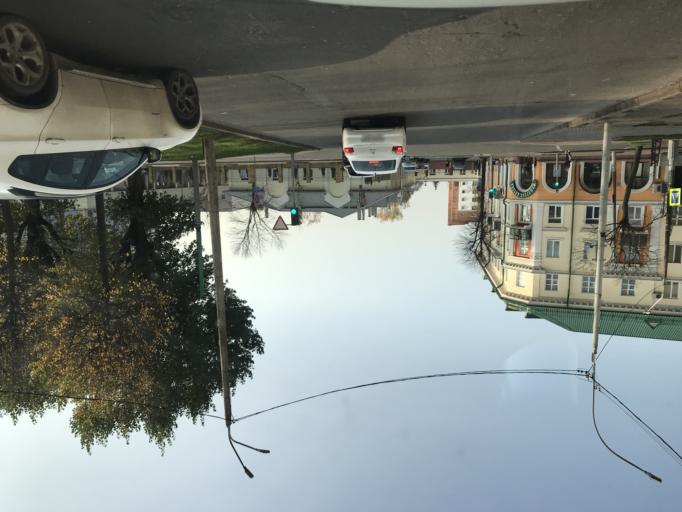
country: BY
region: Mogilev
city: Mahilyow
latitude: 53.9019
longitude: 30.3420
